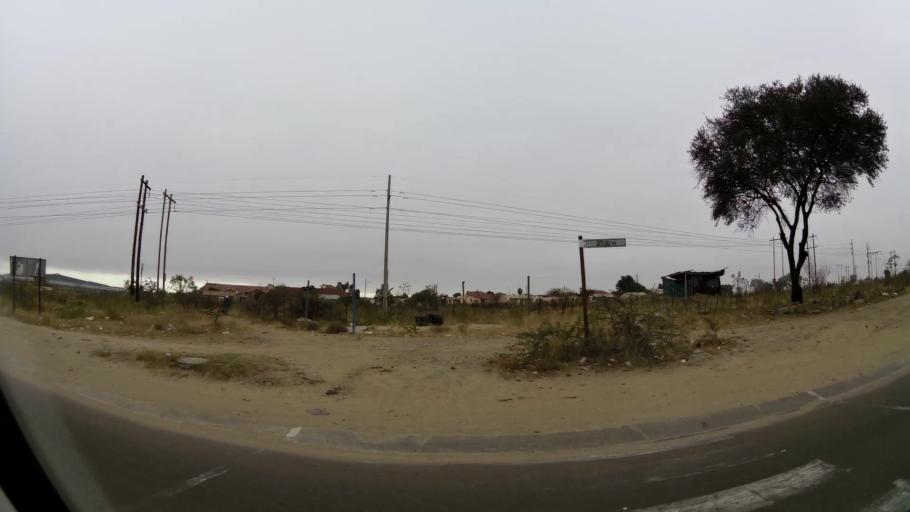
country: ZA
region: Limpopo
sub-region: Capricorn District Municipality
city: Polokwane
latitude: -23.8401
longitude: 29.4001
